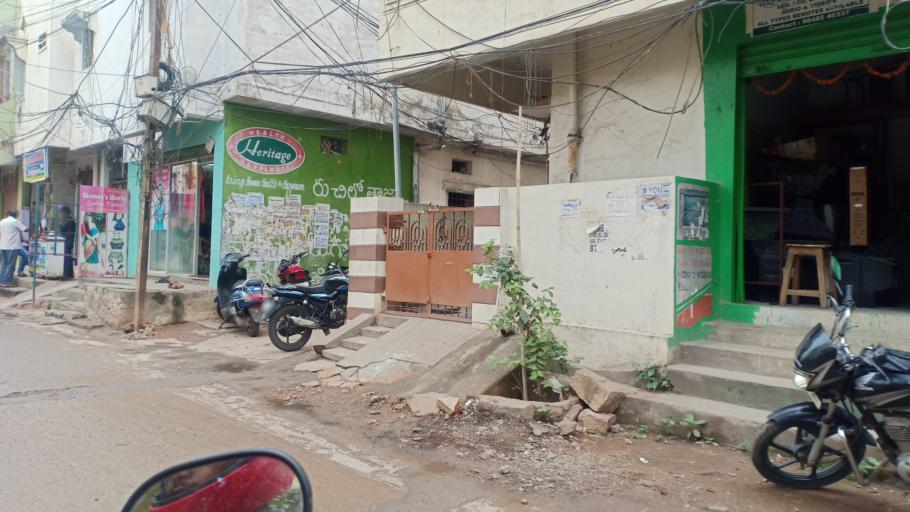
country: IN
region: Telangana
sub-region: Hyderabad
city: Hyderabad
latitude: 17.4325
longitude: 78.4414
